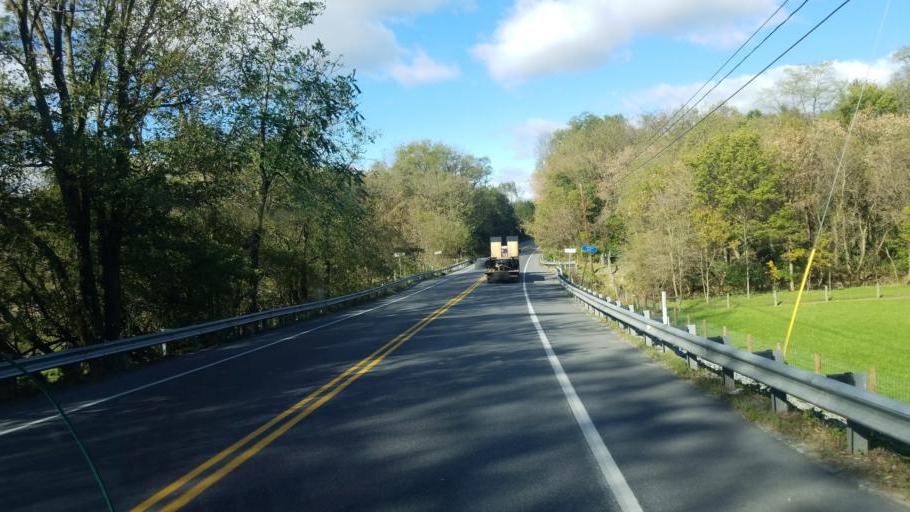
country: US
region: Pennsylvania
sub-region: Franklin County
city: Waynesboro
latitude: 39.7709
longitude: -77.6471
